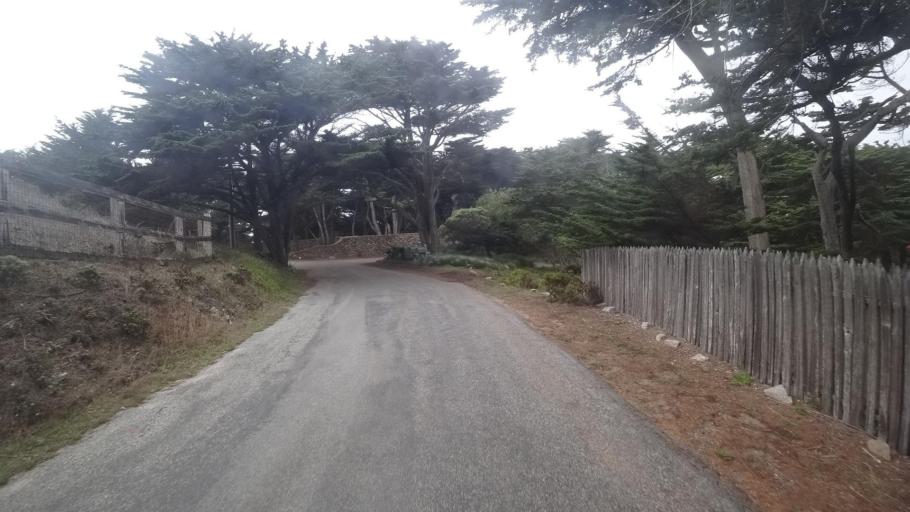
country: US
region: California
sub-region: Monterey County
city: Carmel-by-the-Sea
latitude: 36.4916
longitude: -121.9426
